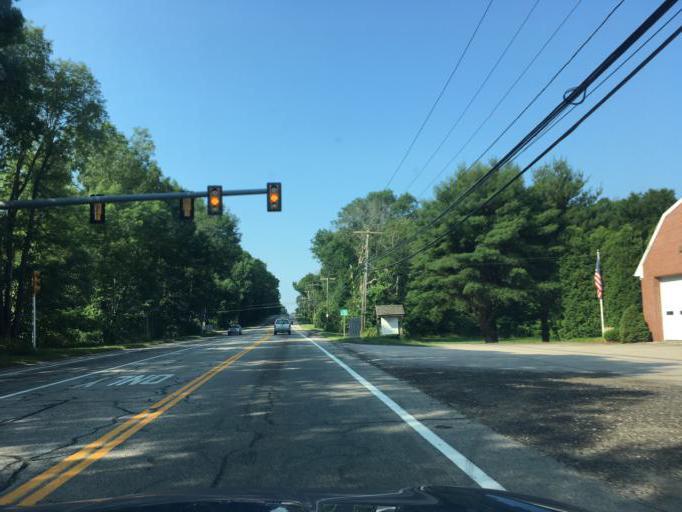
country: US
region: Rhode Island
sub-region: Washington County
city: Exeter
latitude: 41.5335
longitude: -71.5468
